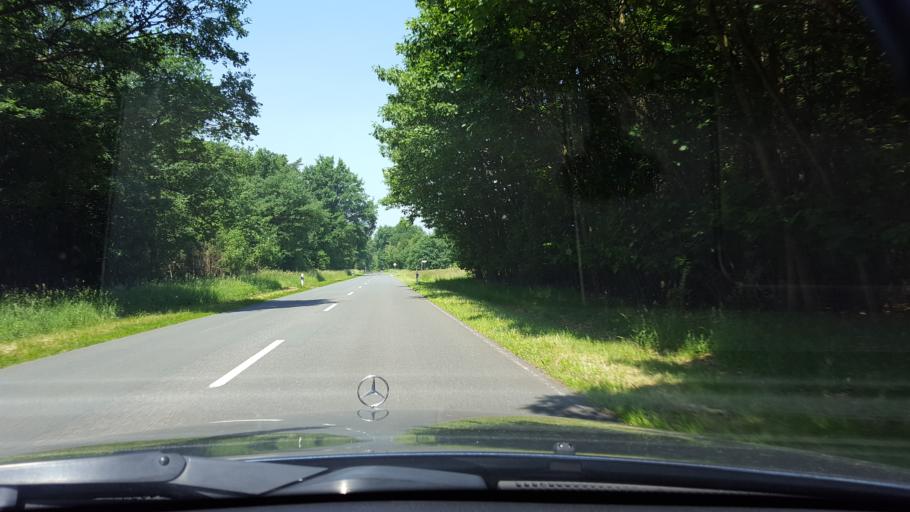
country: DE
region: North Rhine-Westphalia
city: Olfen
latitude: 51.7147
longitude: 7.3100
